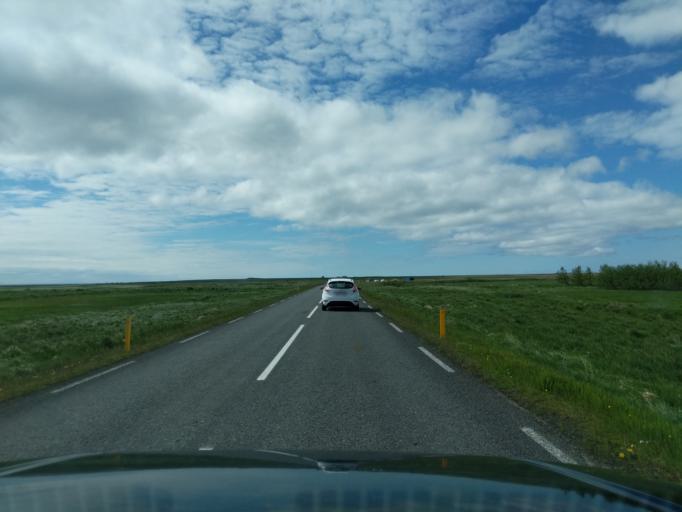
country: IS
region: West
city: Stykkisholmur
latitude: 64.8350
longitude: -22.9693
